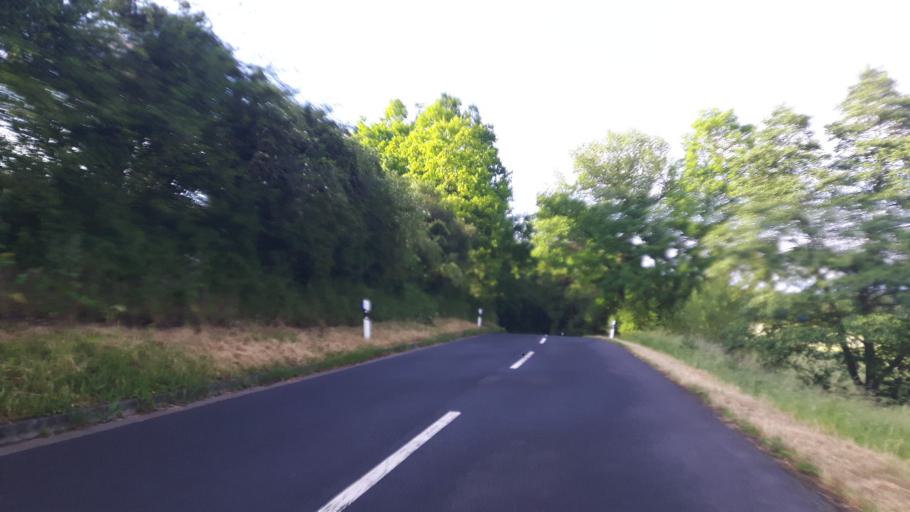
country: DE
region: Bavaria
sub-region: Regierungsbezirk Unterfranken
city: Sulzfeld
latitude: 50.2205
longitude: 10.3954
